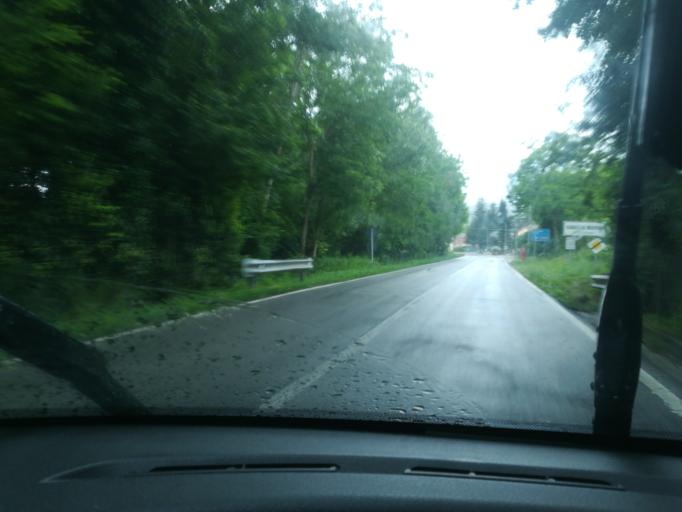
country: IT
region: The Marches
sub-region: Provincia di Macerata
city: Sarnano
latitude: 43.0549
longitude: 13.2737
